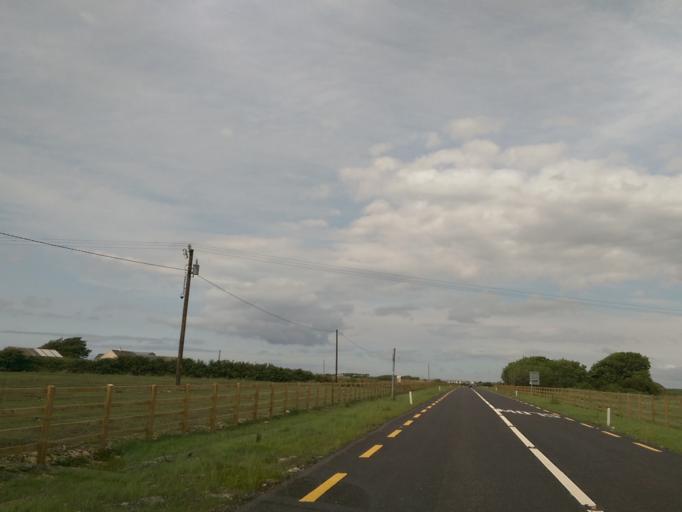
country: IE
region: Munster
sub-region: An Clar
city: Kilrush
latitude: 52.7386
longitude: -9.4821
